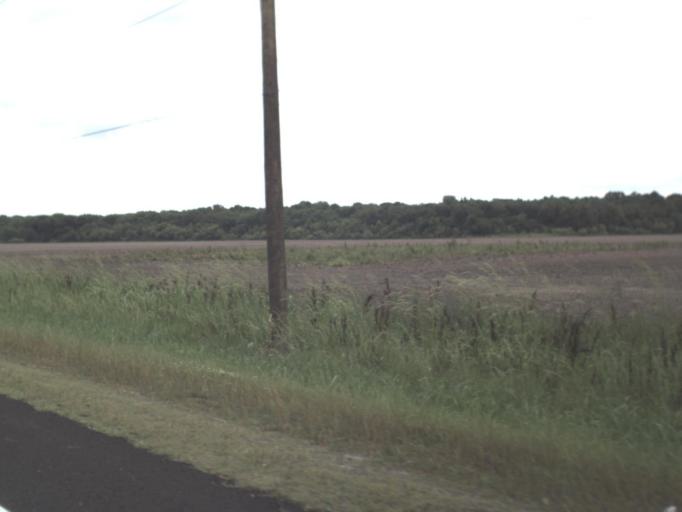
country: US
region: Florida
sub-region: Nassau County
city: Callahan
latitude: 30.6190
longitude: -81.8438
